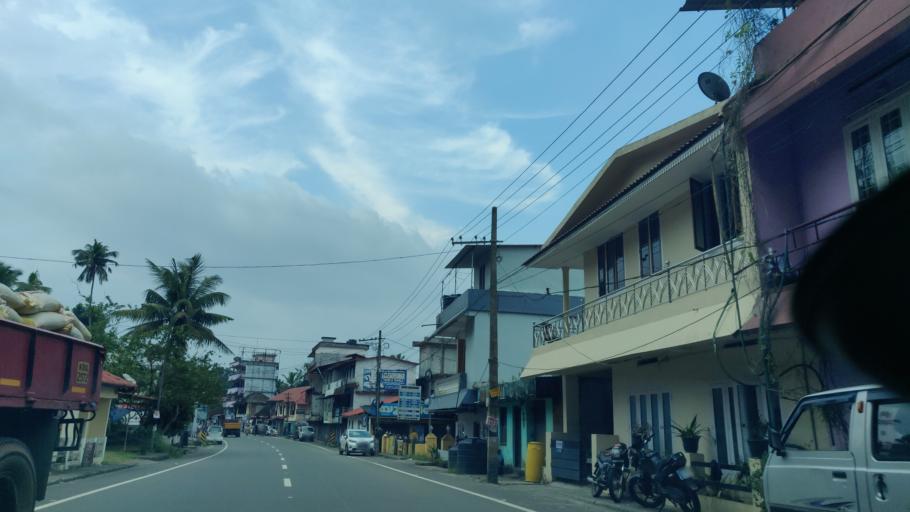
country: IN
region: Kerala
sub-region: Kottayam
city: Palackattumala
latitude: 9.8505
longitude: 76.6864
